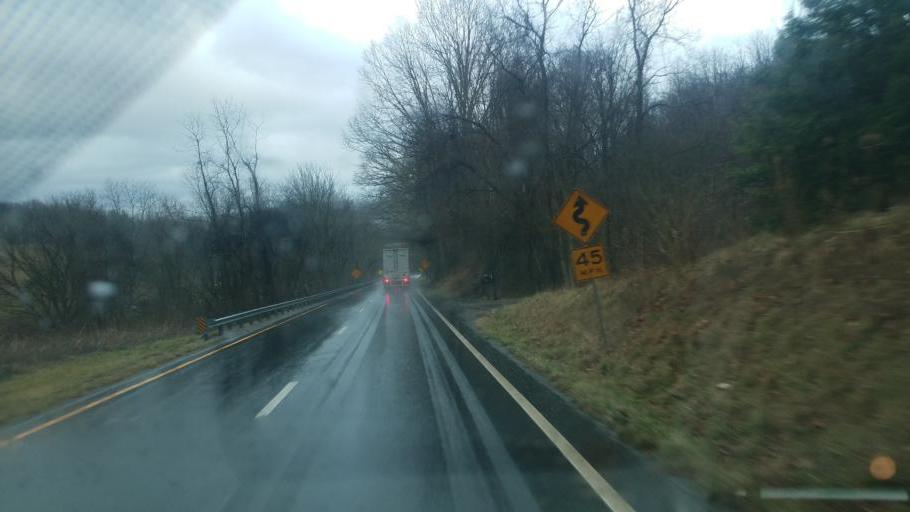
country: US
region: Virginia
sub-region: Giles County
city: Pearisburg
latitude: 37.2945
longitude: -80.7419
